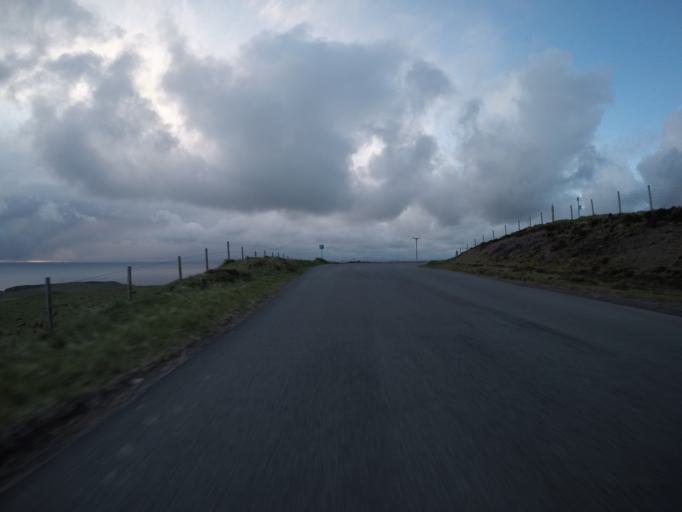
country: GB
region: Scotland
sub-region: Highland
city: Portree
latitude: 57.6017
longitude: -6.3777
